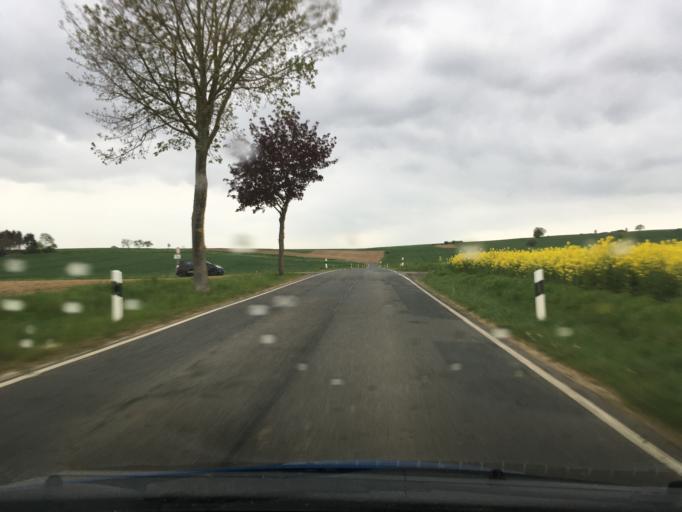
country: DE
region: Lower Saxony
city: Eimen
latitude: 51.8638
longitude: 9.8085
